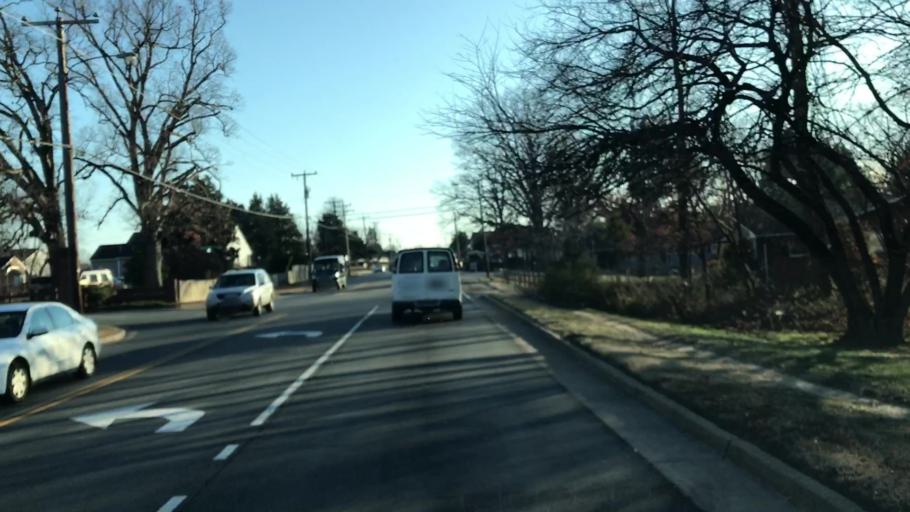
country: US
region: Virginia
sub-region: City of Fredericksburg
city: Fredericksburg
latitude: 38.2810
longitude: -77.4812
